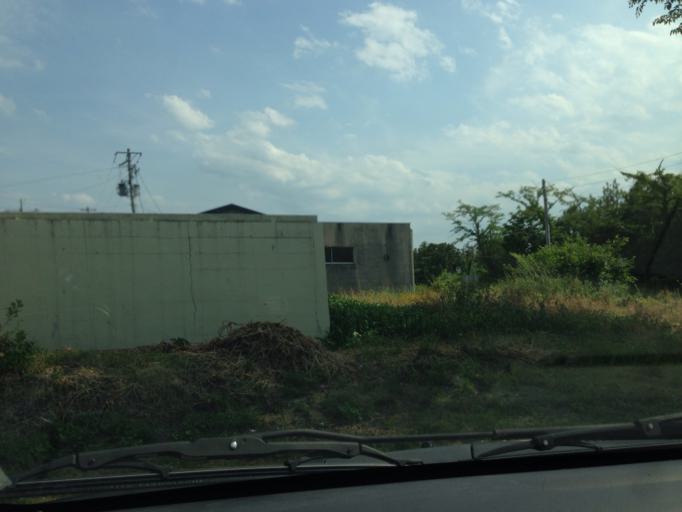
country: JP
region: Fukushima
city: Kitakata
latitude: 37.5172
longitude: 139.8288
